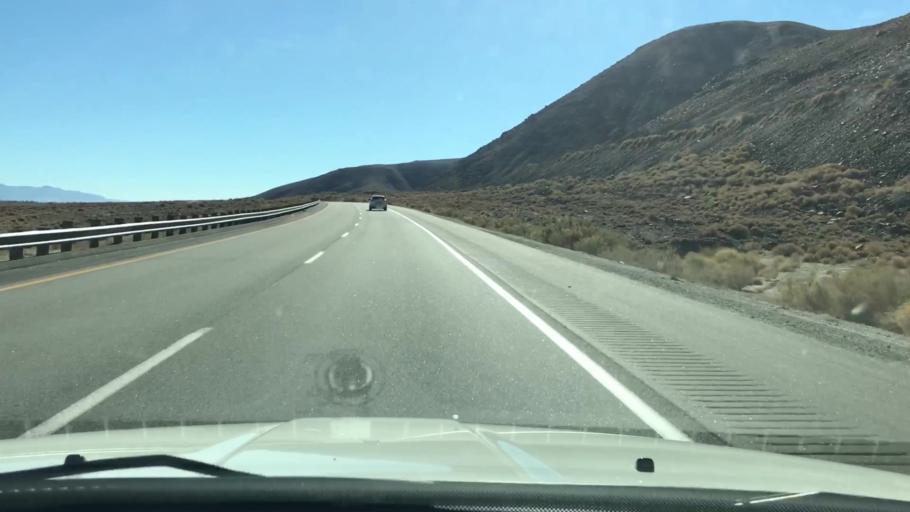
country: US
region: California
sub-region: Inyo County
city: Lone Pine
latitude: 36.6573
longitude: -118.0957
